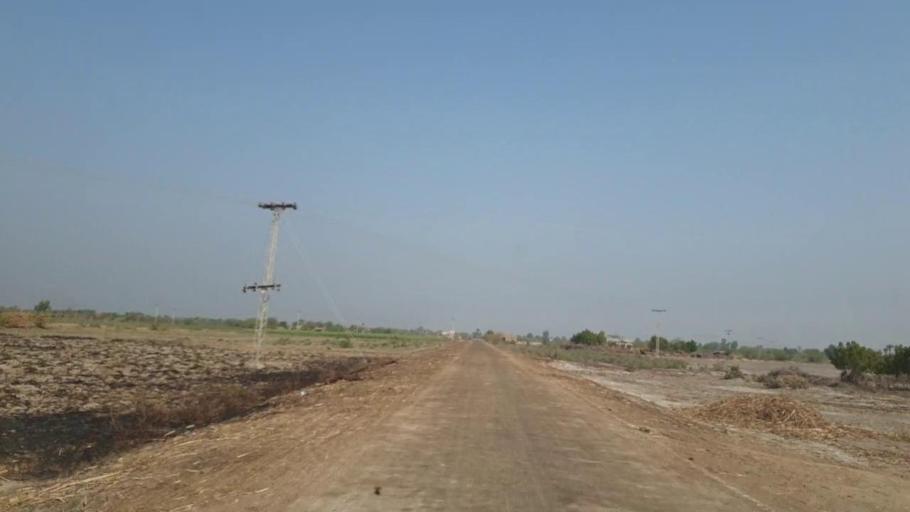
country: PK
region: Sindh
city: Mirpur Khas
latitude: 25.5918
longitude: 69.0148
